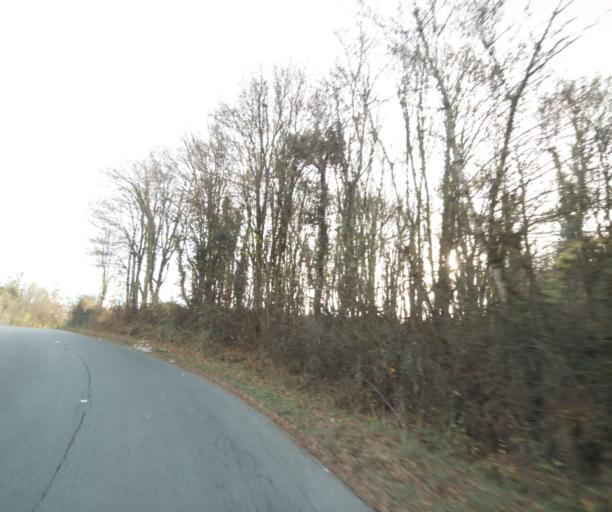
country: FR
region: Poitou-Charentes
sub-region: Departement de la Charente-Maritime
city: Chaniers
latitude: 45.7437
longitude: -0.5429
